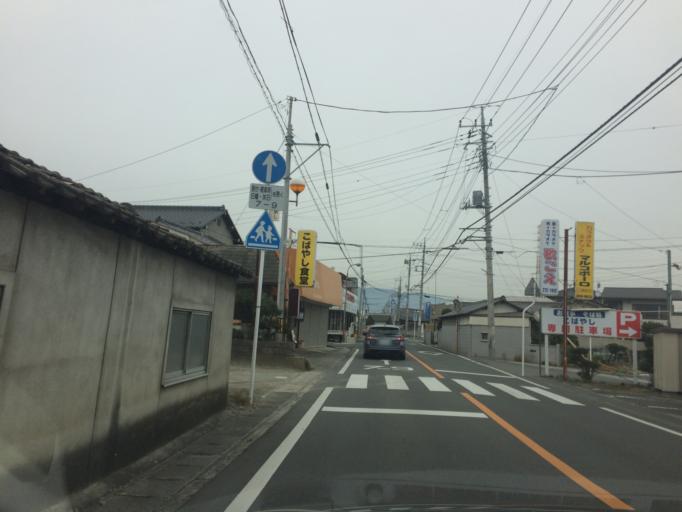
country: JP
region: Yamanashi
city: Ryuo
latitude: 35.6260
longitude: 138.5404
